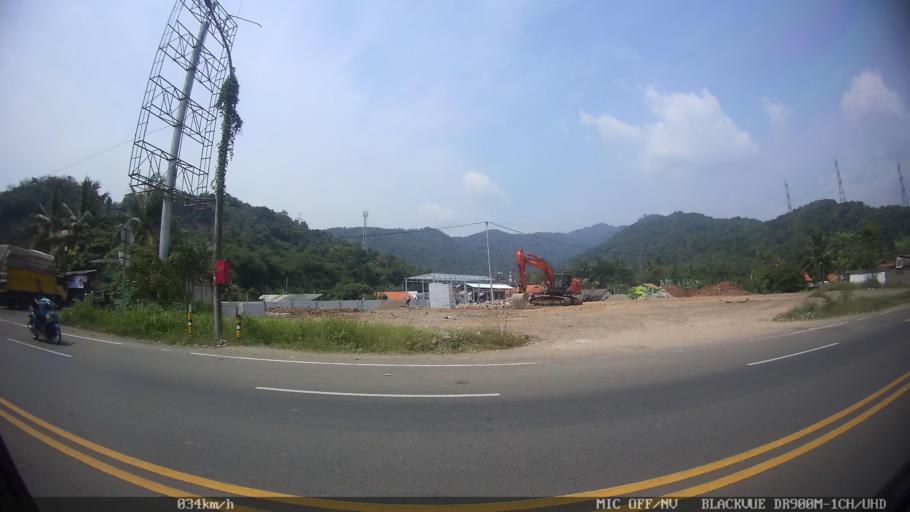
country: ID
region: Banten
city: Curug
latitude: -5.9554
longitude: 106.0029
